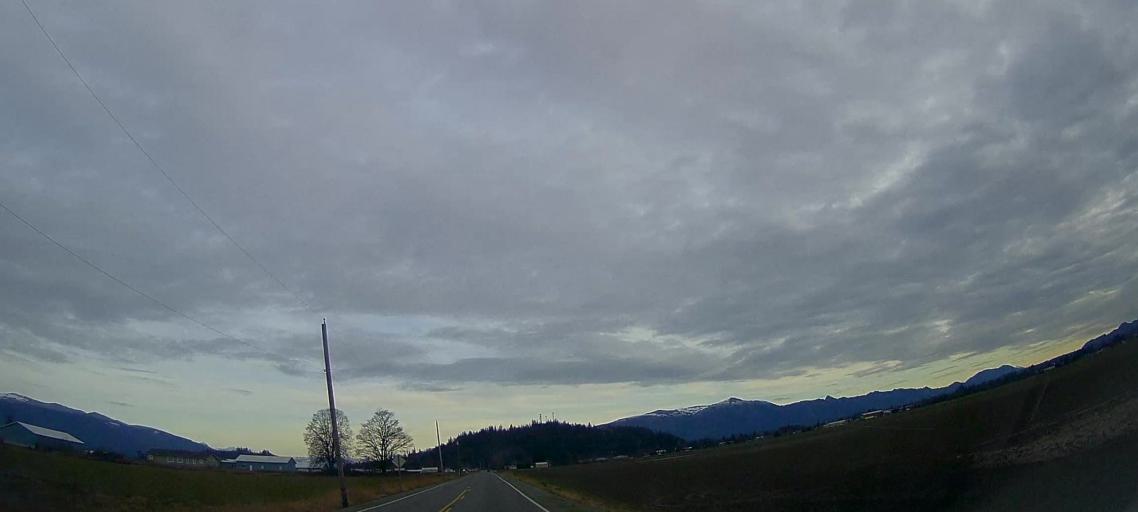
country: US
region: Washington
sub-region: Skagit County
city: Burlington
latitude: 48.4862
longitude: -122.3552
